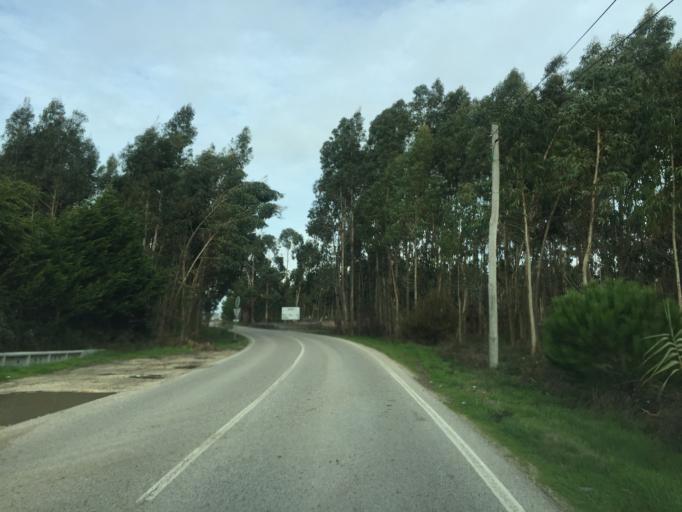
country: PT
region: Coimbra
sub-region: Figueira da Foz
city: Lavos
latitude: 40.0506
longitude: -8.8155
